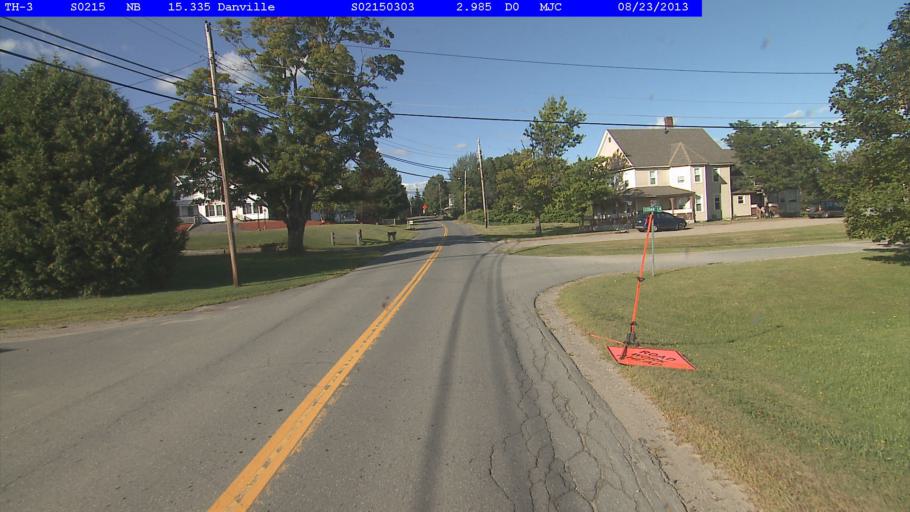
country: US
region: Vermont
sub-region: Caledonia County
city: Saint Johnsbury
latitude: 44.4074
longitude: -72.1409
